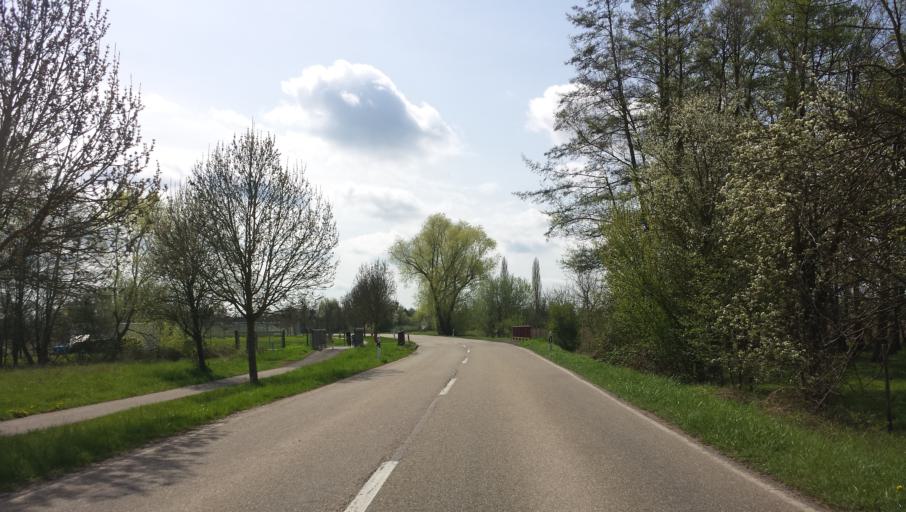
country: DE
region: Rheinland-Pfalz
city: Venningen
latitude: 49.2754
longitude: 8.1733
